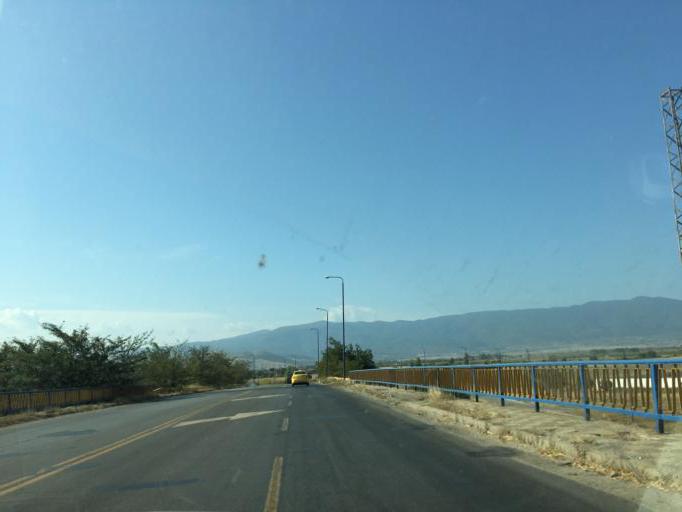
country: BG
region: Pazardzhik
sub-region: Obshtina Pazardzhik
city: Pazardzhik
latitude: 42.1714
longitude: 24.3166
